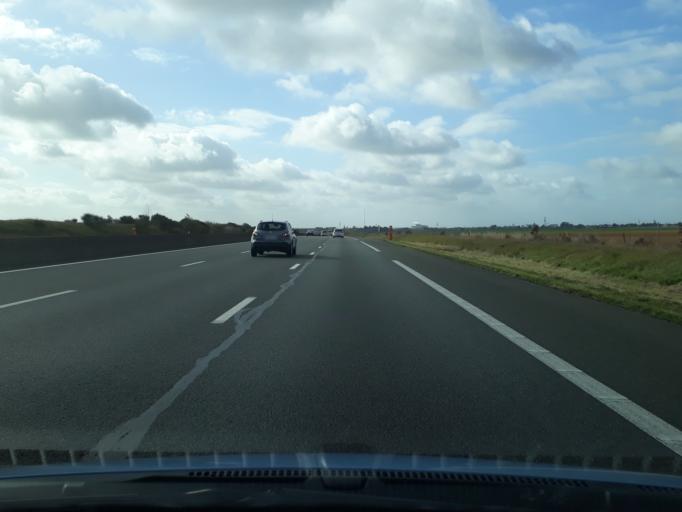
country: FR
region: Centre
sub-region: Departement du Loir-et-Cher
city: La Chaussee-Saint-Victor
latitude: 47.6394
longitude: 1.3602
